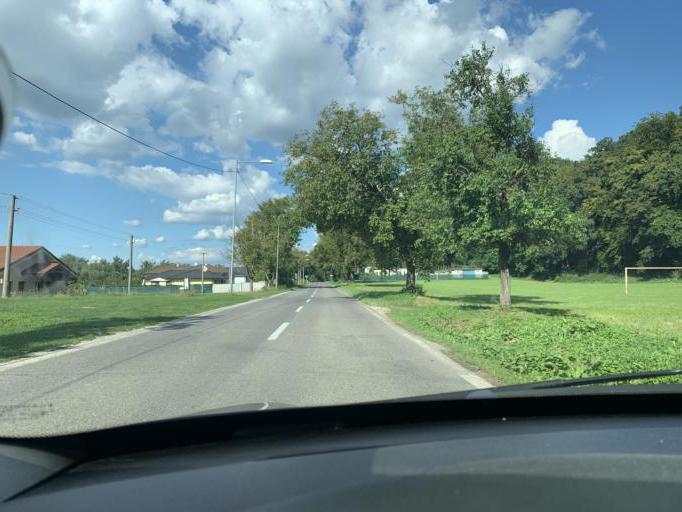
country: SK
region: Trenciansky
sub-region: Okres Trencin
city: Trencin
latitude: 48.8246
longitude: 17.9412
